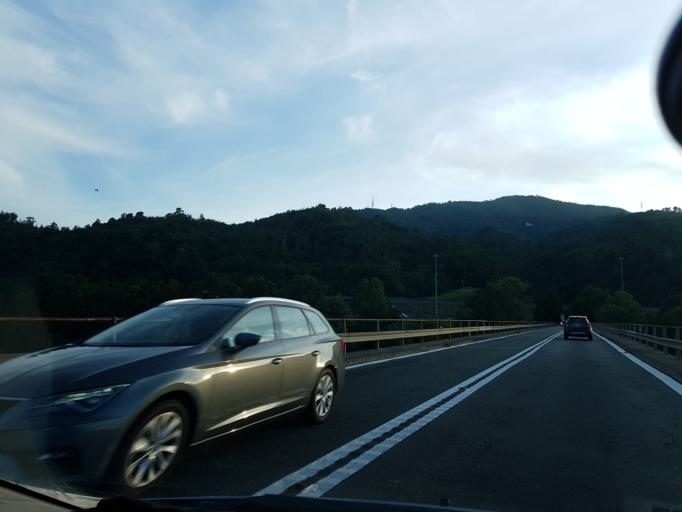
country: IT
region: Tuscany
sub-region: Provincia di Massa-Carrara
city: Terrarossa
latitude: 44.2189
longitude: 9.9632
